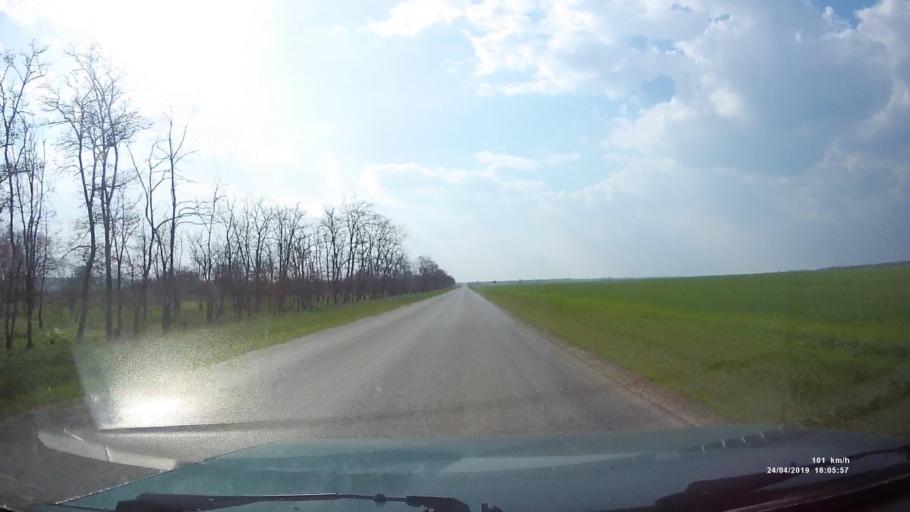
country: RU
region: Rostov
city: Sovetskoye
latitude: 46.6839
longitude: 42.3592
